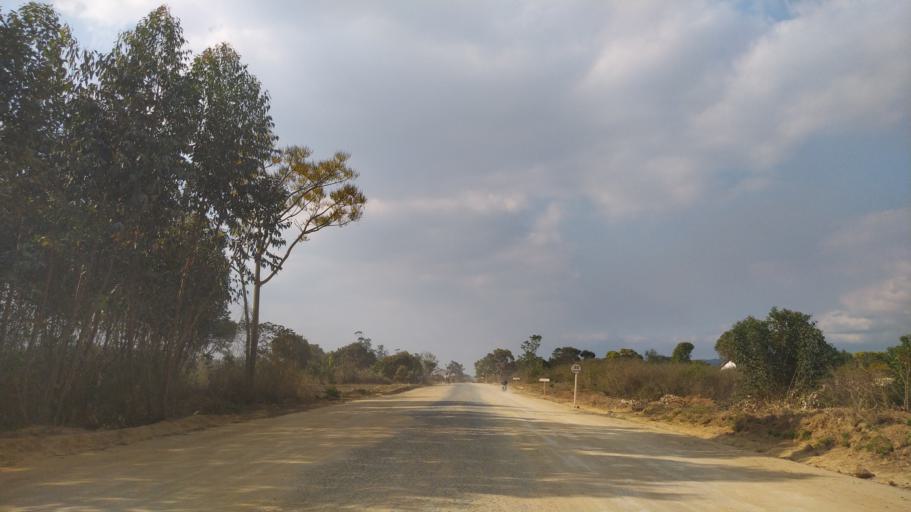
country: MG
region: Alaotra Mangoro
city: Moramanga
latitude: -18.6385
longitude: 48.2758
